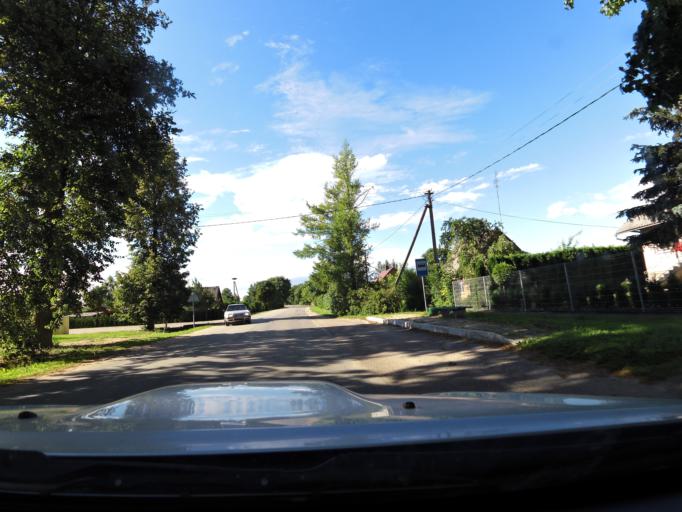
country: LT
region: Panevezys
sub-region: Birzai
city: Birzai
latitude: 56.2716
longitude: 24.8239
